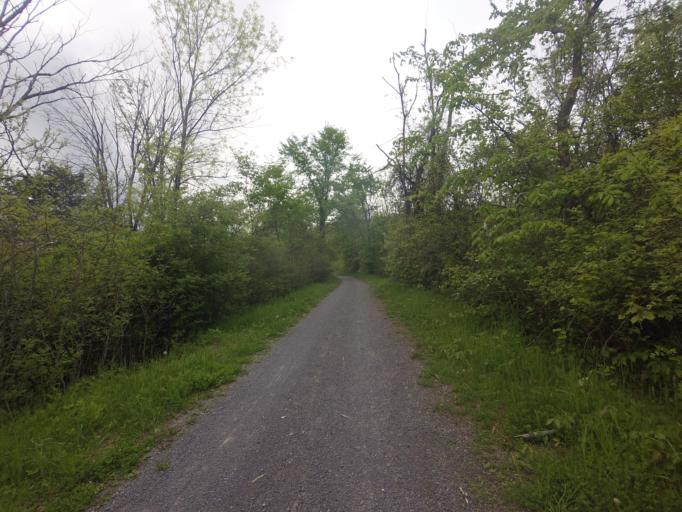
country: CA
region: Ontario
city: Kingston
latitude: 44.3039
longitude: -76.5613
